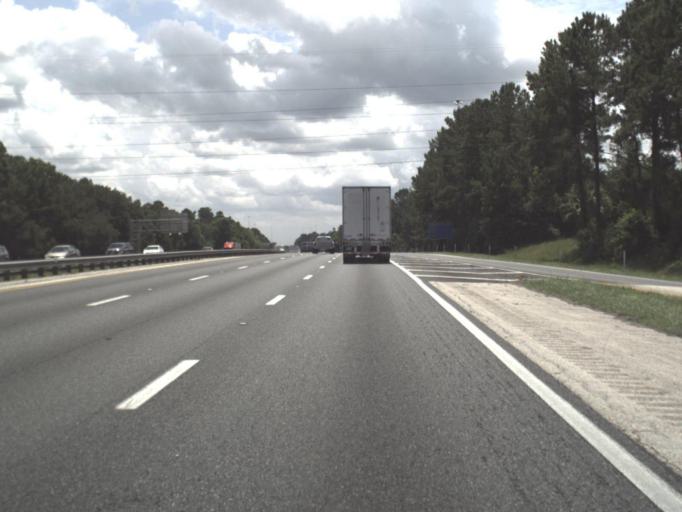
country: US
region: Florida
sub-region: Alachua County
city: Gainesville
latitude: 29.6145
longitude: -82.3843
